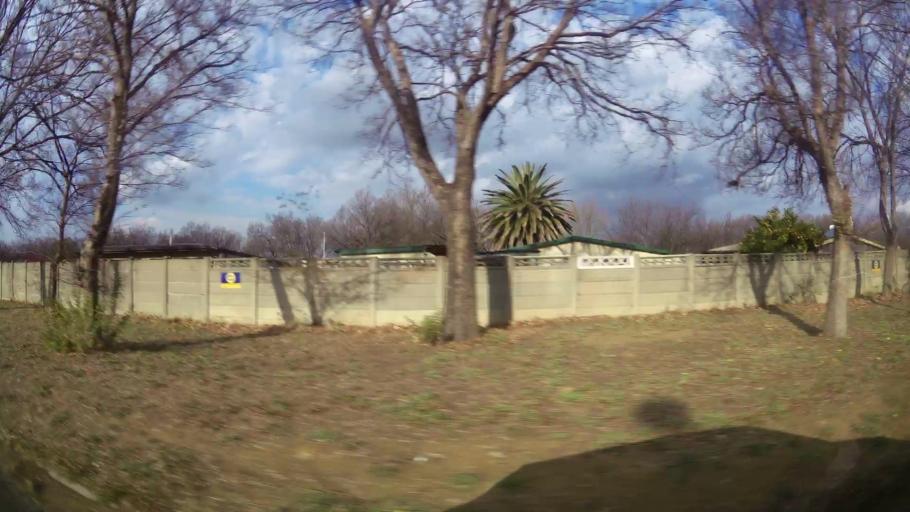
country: ZA
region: Orange Free State
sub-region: Fezile Dabi District Municipality
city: Sasolburg
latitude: -26.8073
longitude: 27.8113
